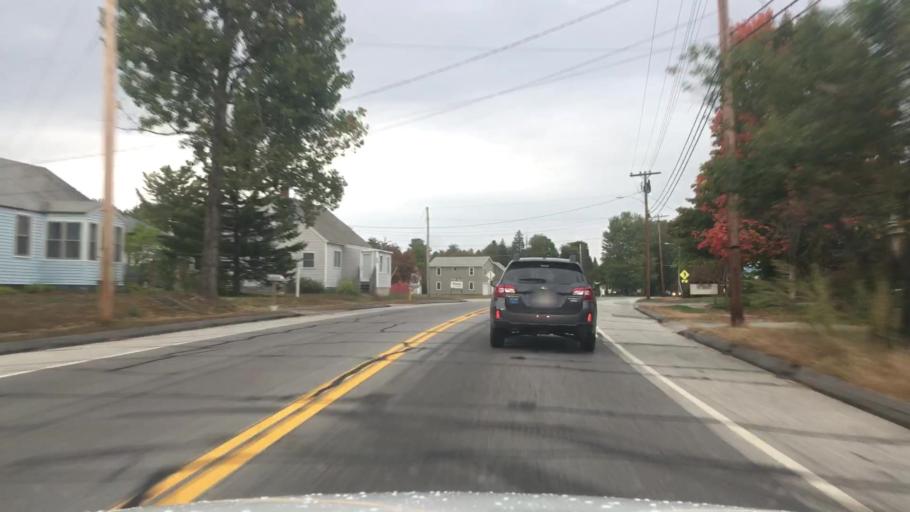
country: US
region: Maine
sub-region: York County
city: Waterboro
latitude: 43.5313
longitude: -70.7186
